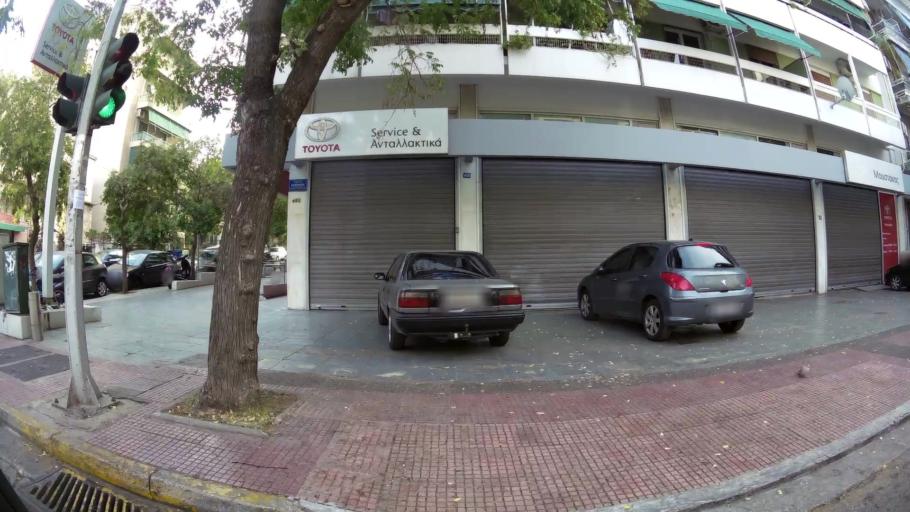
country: GR
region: Attica
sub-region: Nomarchia Athinas
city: Nea Chalkidona
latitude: 38.0239
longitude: 23.7308
